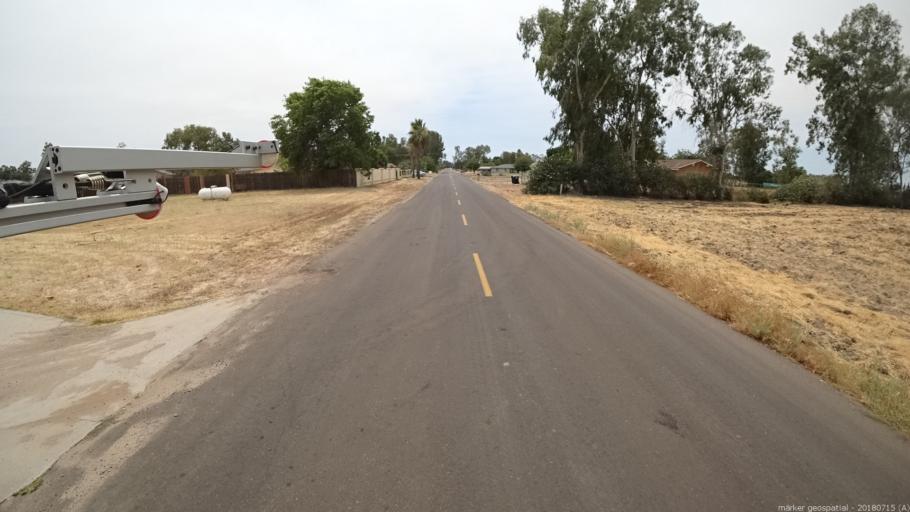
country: US
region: California
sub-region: Madera County
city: Madera Acres
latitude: 37.0156
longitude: -120.0893
